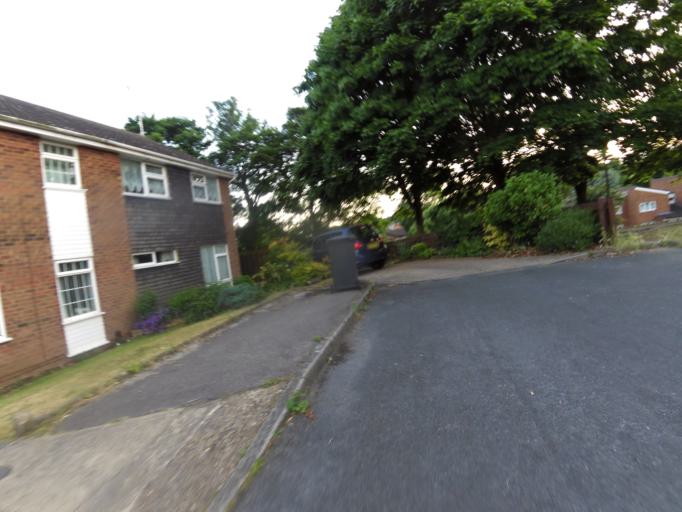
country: GB
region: England
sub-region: Suffolk
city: Ipswich
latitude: 52.0406
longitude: 1.1388
